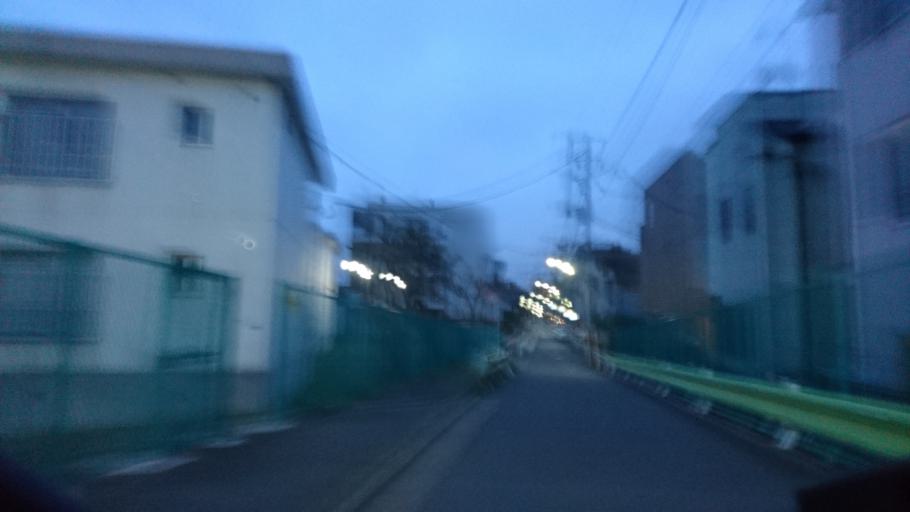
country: JP
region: Kanagawa
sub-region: Kawasaki-shi
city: Kawasaki
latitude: 35.5600
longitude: 139.7283
